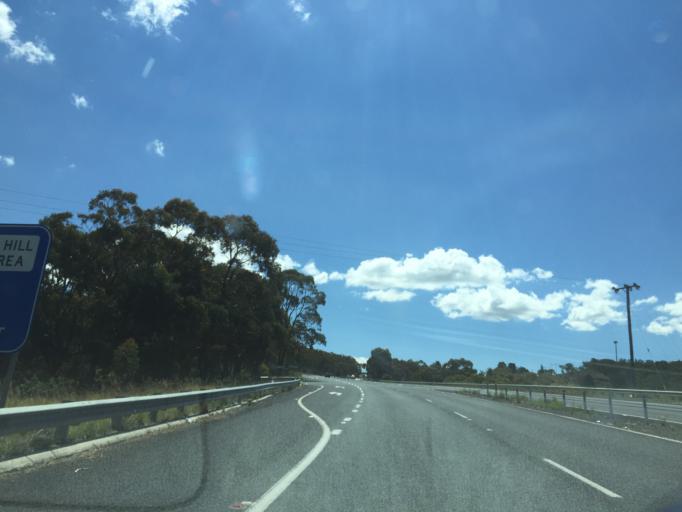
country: AU
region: New South Wales
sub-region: Lithgow
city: Lithgow
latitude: -33.4314
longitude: 150.1104
